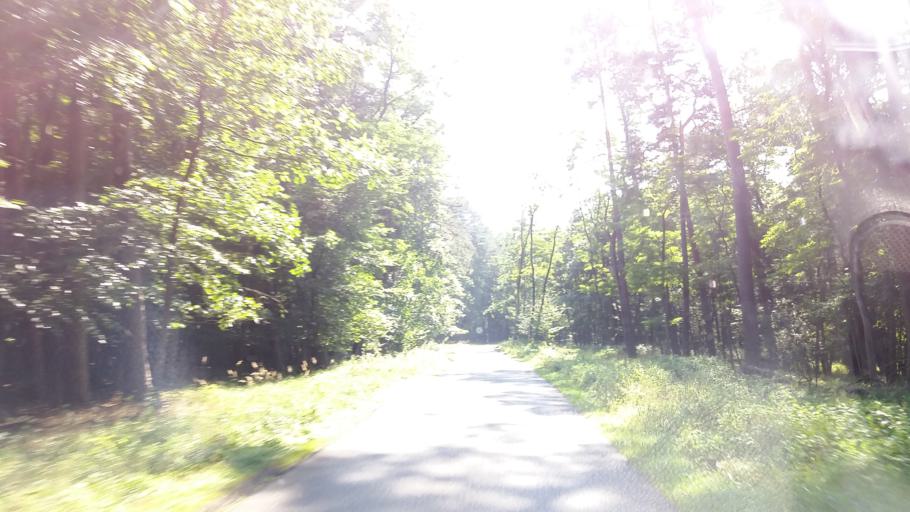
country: PL
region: West Pomeranian Voivodeship
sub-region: Powiat walecki
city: Czlopa
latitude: 53.0608
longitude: 15.9418
